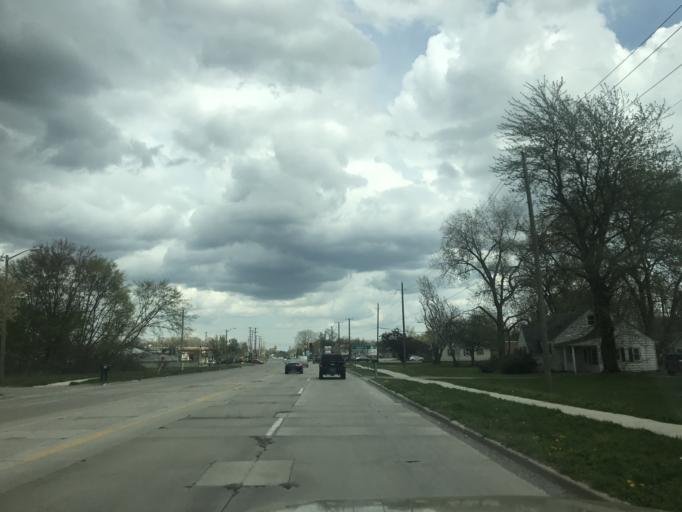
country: US
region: Michigan
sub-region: Wayne County
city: Taylor
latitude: 42.1958
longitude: -83.3095
